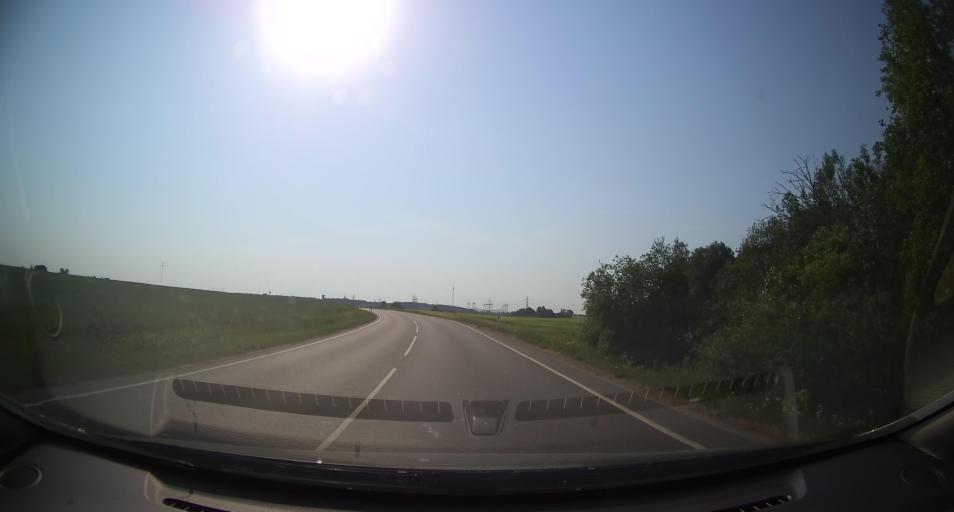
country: EE
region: Harju
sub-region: Raasiku vald
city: Arukula
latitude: 59.3667
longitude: 25.0274
